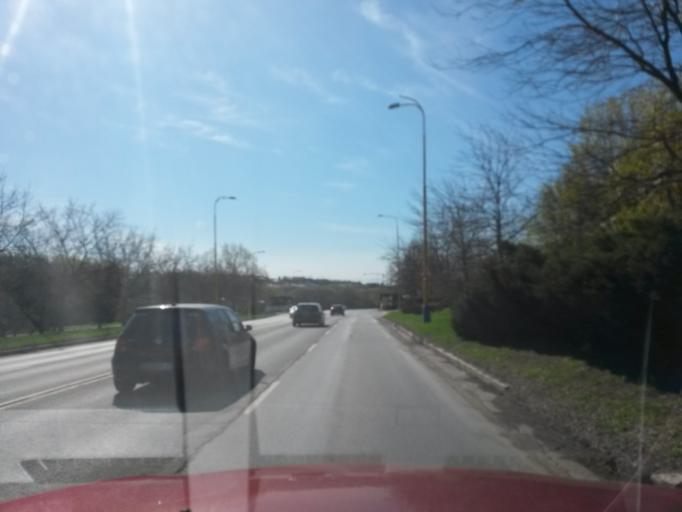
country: SK
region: Kosicky
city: Kosice
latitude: 48.7107
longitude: 21.2174
